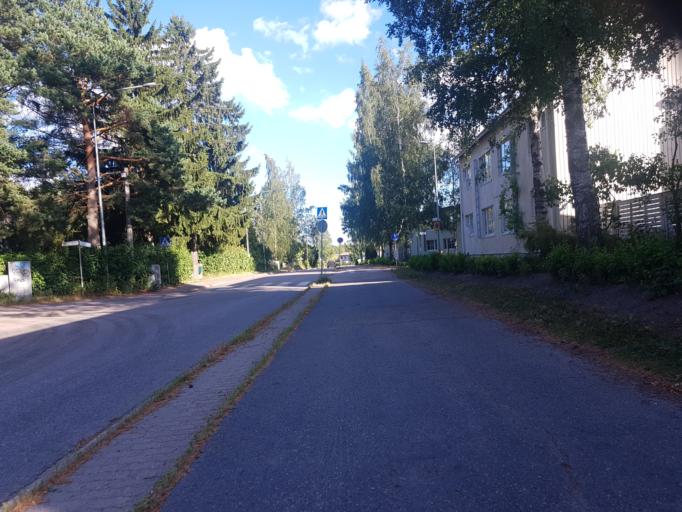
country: FI
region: Uusimaa
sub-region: Helsinki
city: Vantaa
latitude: 60.2705
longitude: 25.0070
